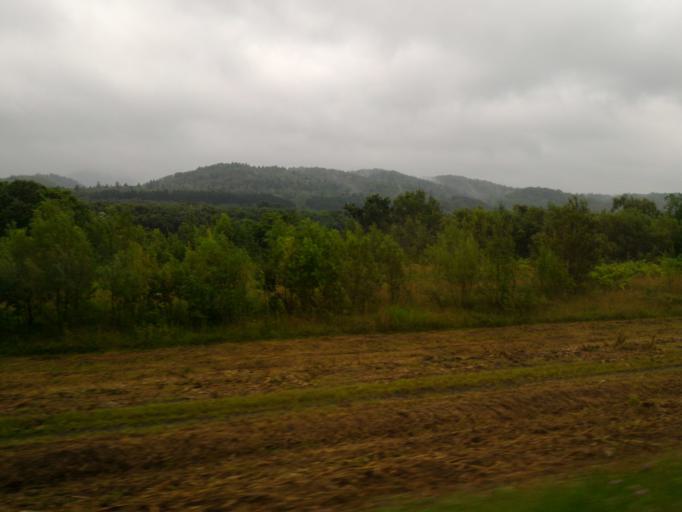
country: JP
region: Hokkaido
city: Nayoro
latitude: 44.7590
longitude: 142.0502
